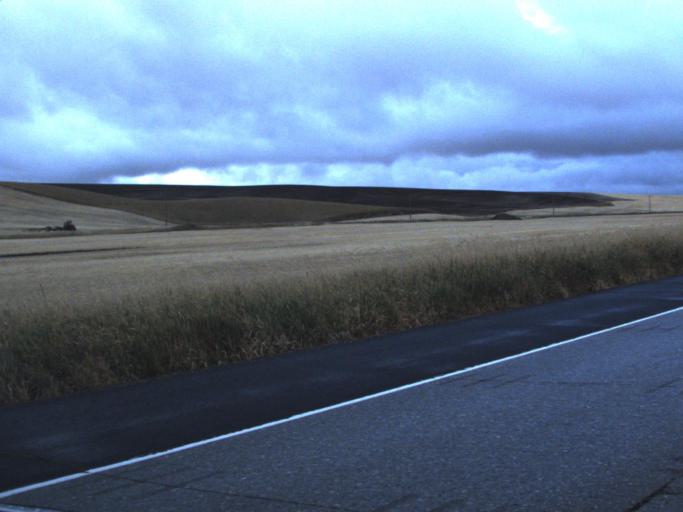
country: US
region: Washington
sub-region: Whitman County
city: Colfax
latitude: 47.0746
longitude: -117.3830
